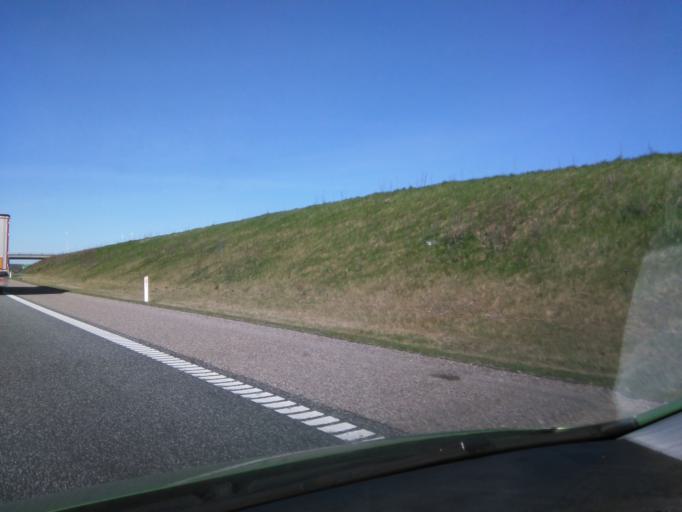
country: DK
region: Central Jutland
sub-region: Hedensted Kommune
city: Torring
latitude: 55.8325
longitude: 9.4780
